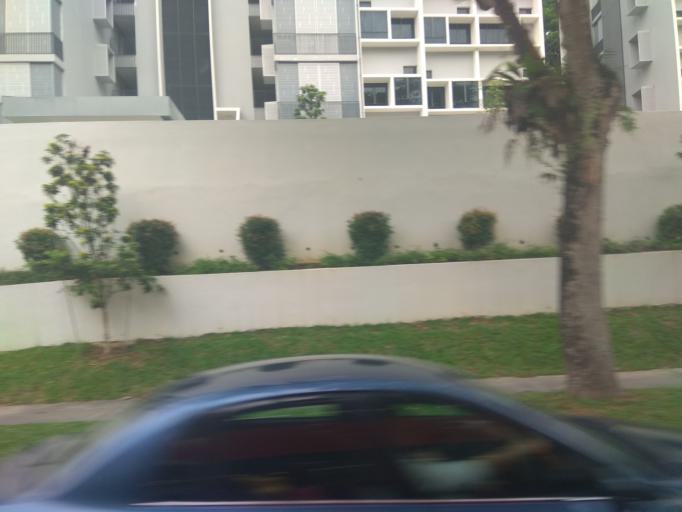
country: MY
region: Johor
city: Johor Bahru
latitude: 1.3536
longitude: 103.6868
